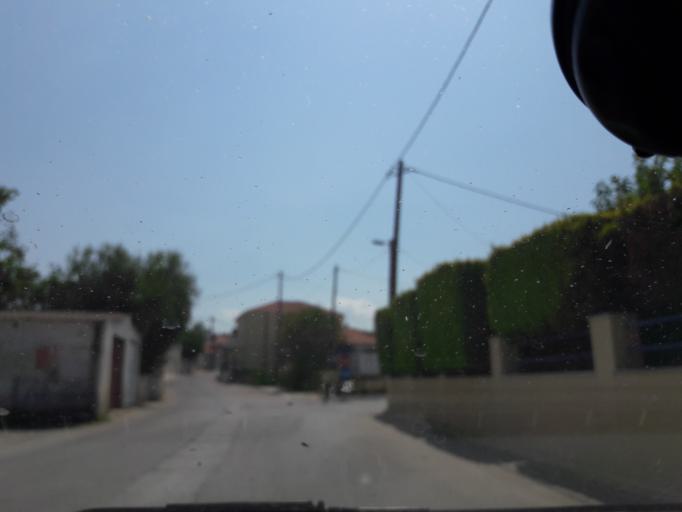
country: GR
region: North Aegean
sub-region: Nomos Lesvou
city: Myrina
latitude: 39.8767
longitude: 25.2720
